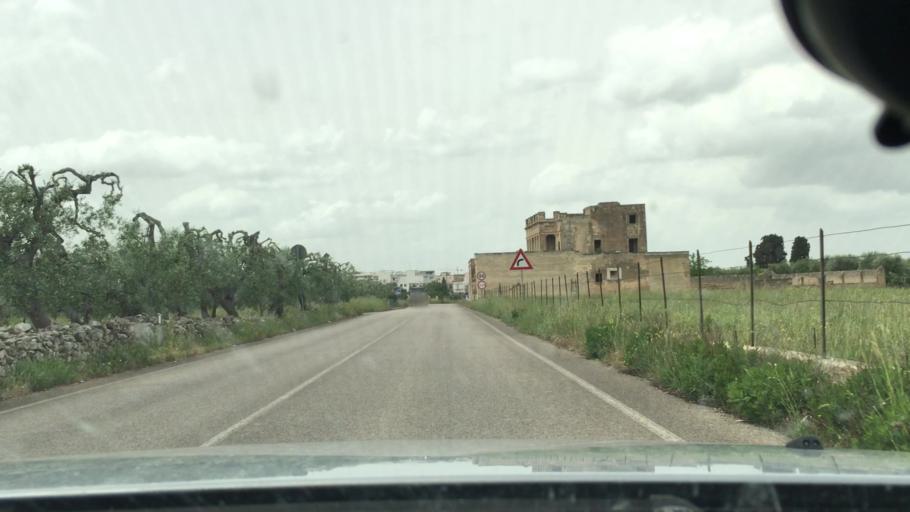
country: IT
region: Apulia
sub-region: Provincia di Bari
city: Capurso
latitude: 41.0431
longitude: 16.9365
